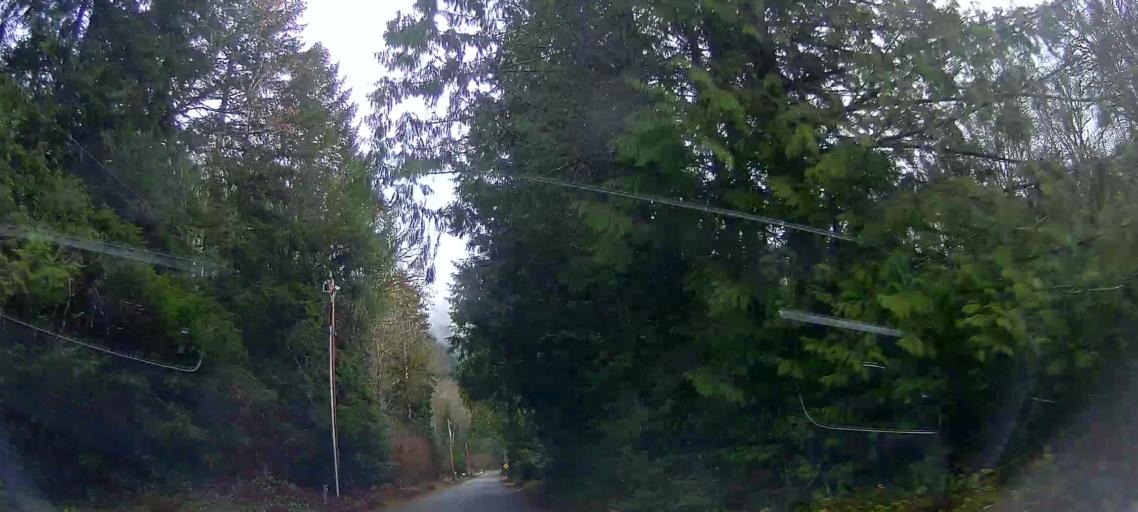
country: US
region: Washington
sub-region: Snohomish County
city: Darrington
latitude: 48.5310
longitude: -121.4043
